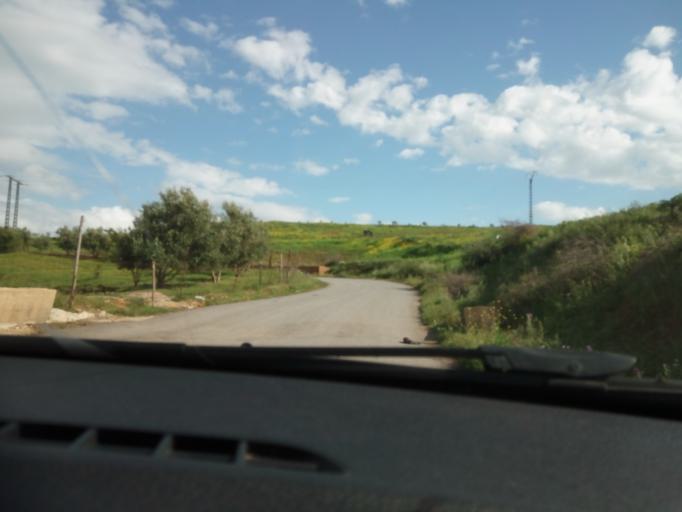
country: DZ
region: Tipaza
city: Hadjout
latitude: 36.3735
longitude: 2.4833
